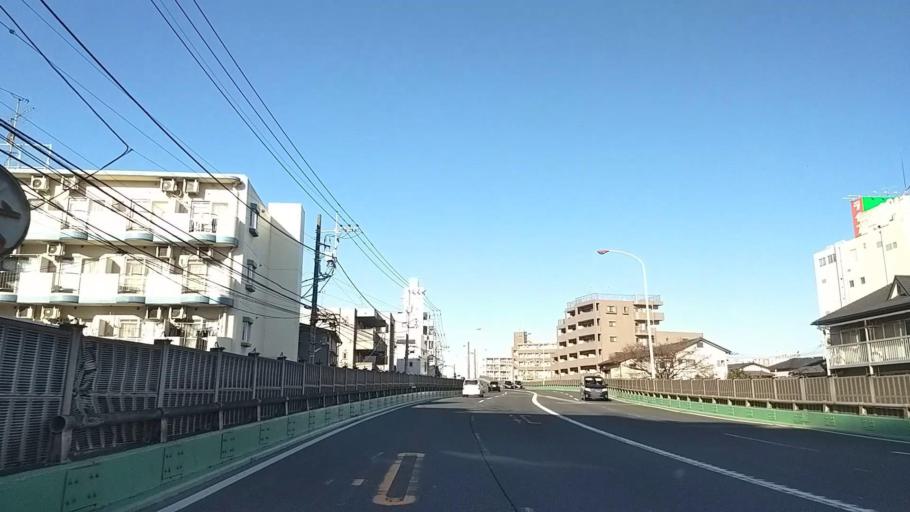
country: JP
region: Tokyo
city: Chofugaoka
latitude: 35.6148
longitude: 139.5650
